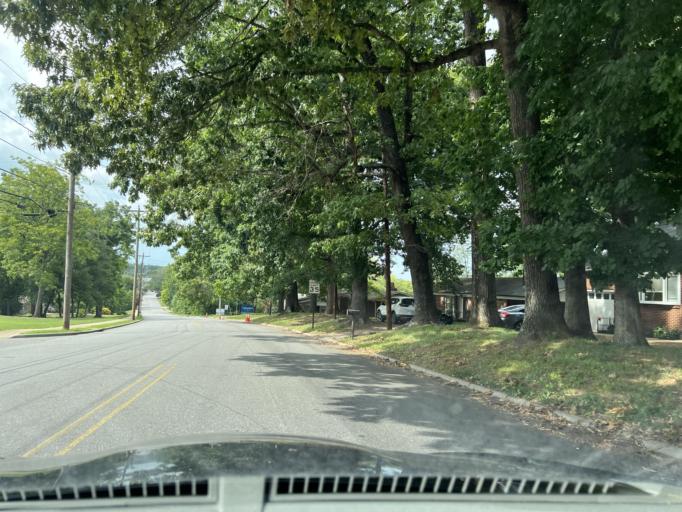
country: US
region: North Carolina
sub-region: Iredell County
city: Statesville
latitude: 35.8016
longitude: -80.8769
